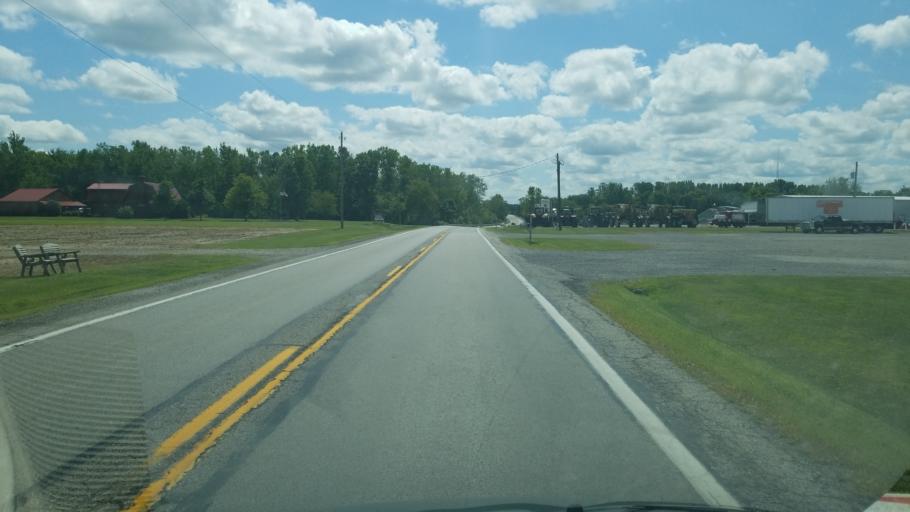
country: US
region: Ohio
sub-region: Henry County
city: Liberty Center
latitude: 41.4199
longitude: -84.0089
